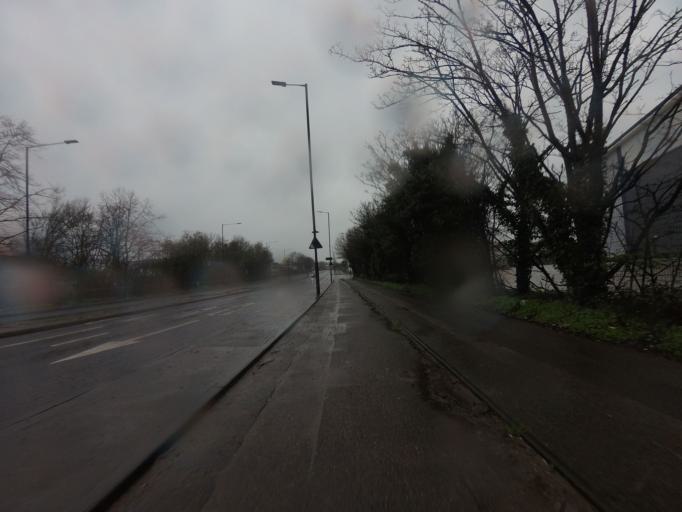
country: GB
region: England
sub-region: Hertfordshire
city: Waltham Cross
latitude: 51.6458
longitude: -0.0313
